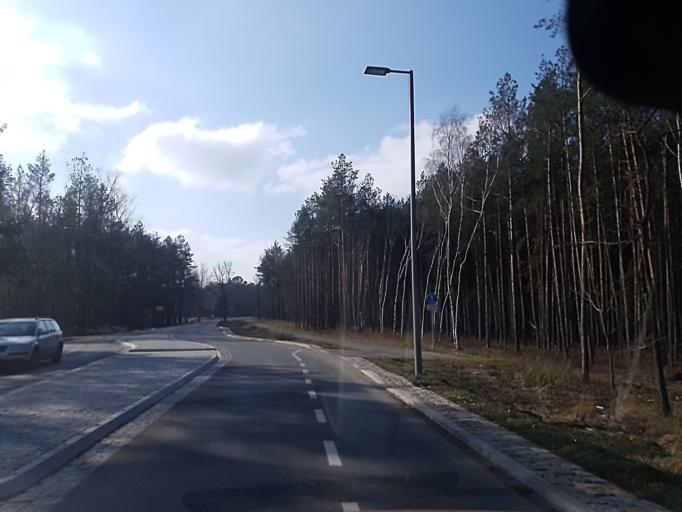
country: DE
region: Brandenburg
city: Doberlug-Kirchhain
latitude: 51.6331
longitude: 13.6040
